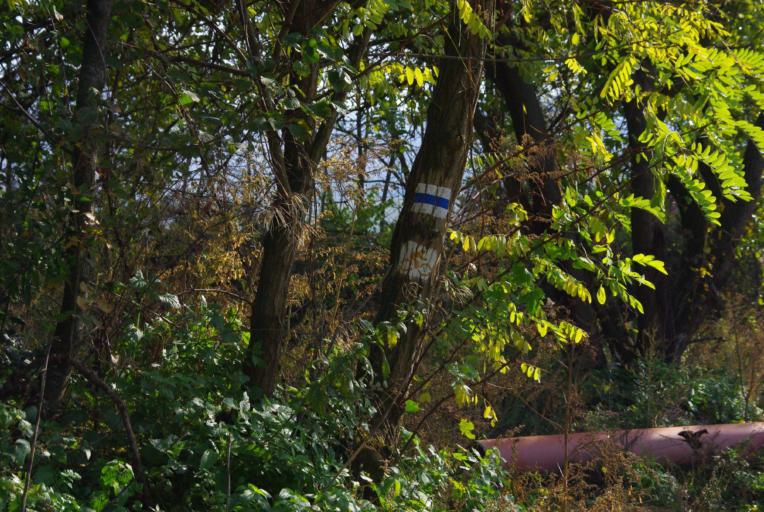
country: HU
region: Komarom-Esztergom
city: Piliscsev
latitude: 47.6827
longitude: 18.8228
